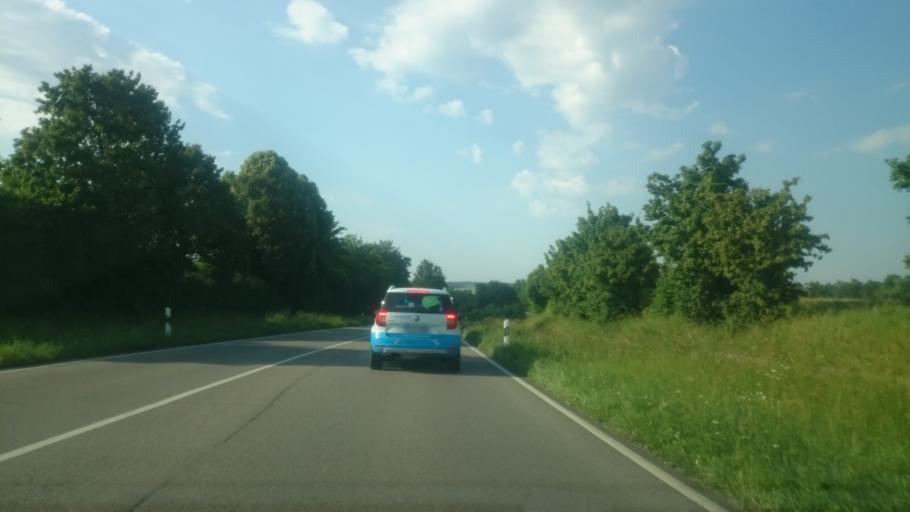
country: DE
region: Baden-Wuerttemberg
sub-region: Tuebingen Region
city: Gomaringen
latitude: 48.4469
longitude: 9.0792
